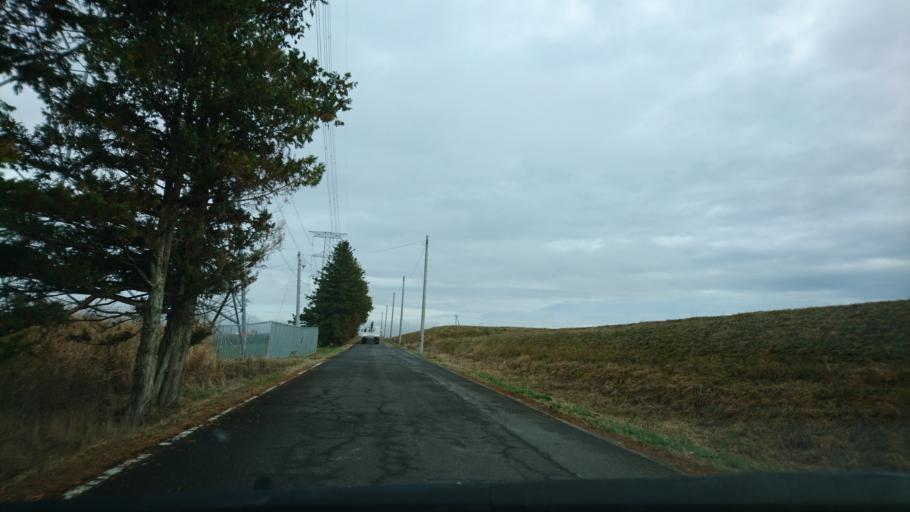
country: JP
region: Iwate
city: Ichinoseki
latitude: 38.8844
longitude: 141.1925
